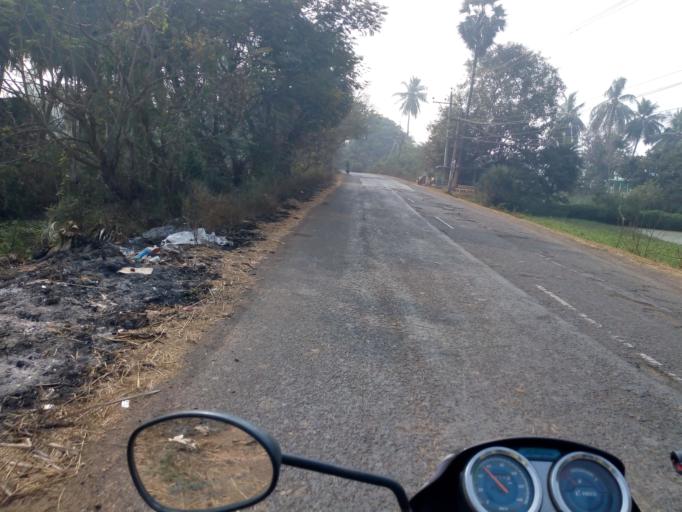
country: IN
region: Andhra Pradesh
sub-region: West Godavari
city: Tadepallegudem
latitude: 16.7820
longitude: 81.4199
